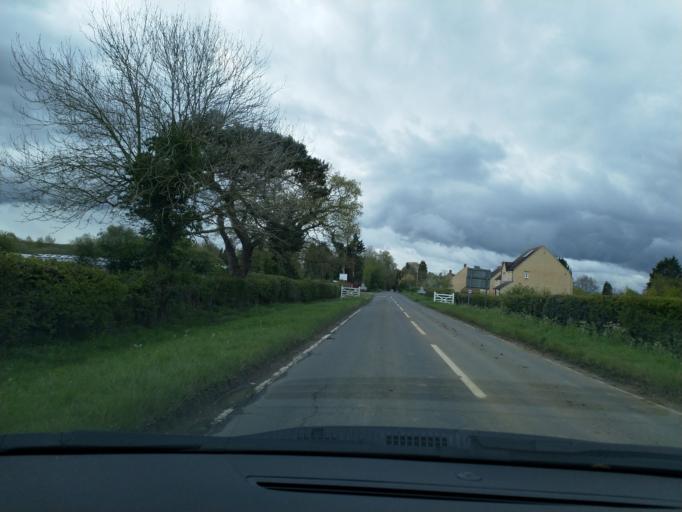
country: GB
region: England
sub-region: Oxfordshire
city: Yarnton
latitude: 51.7988
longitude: -1.3400
